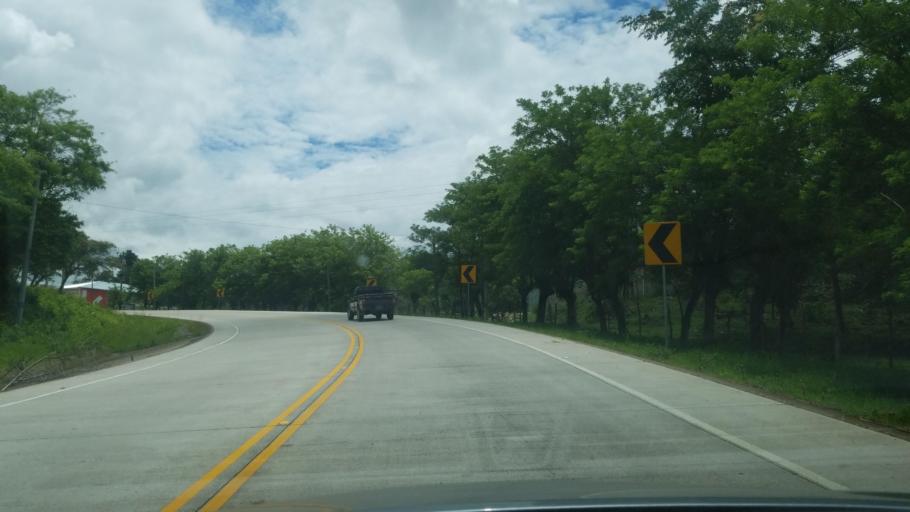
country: HN
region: Copan
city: San Jeronimo
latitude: 14.9848
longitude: -88.8586
